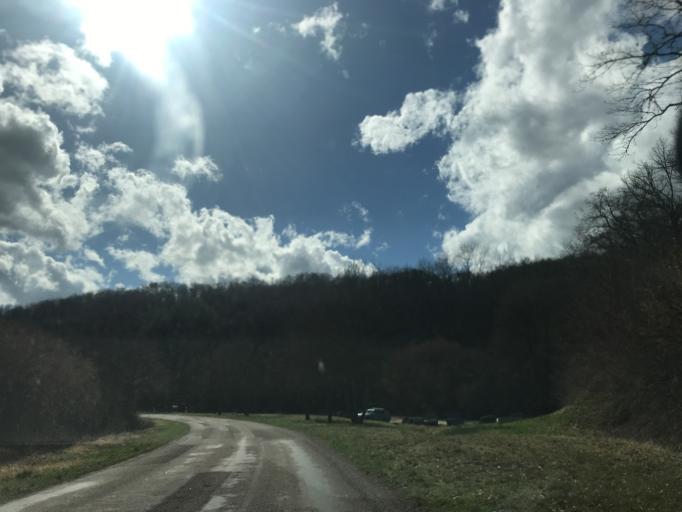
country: FR
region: Bourgogne
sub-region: Departement de la Nievre
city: Clamecy
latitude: 47.4941
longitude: 3.5077
